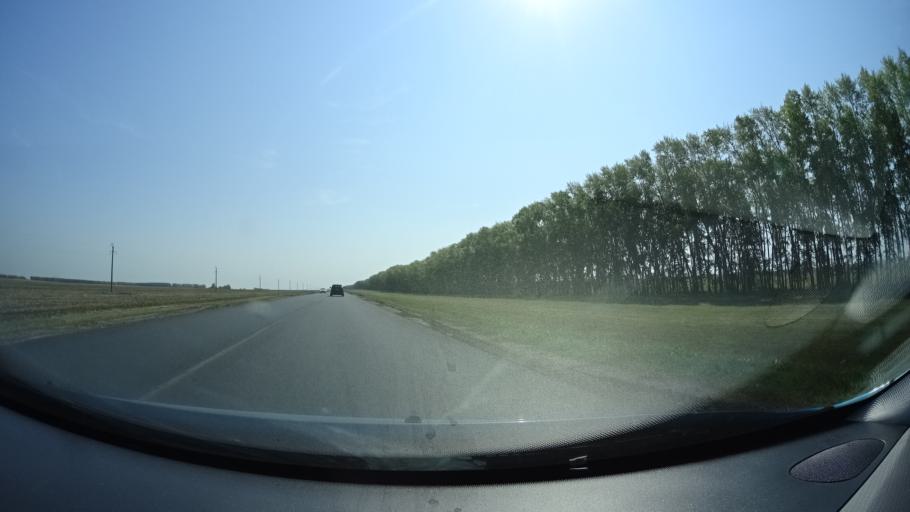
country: RU
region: Bashkortostan
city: Karmaskaly
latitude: 54.4143
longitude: 56.0585
